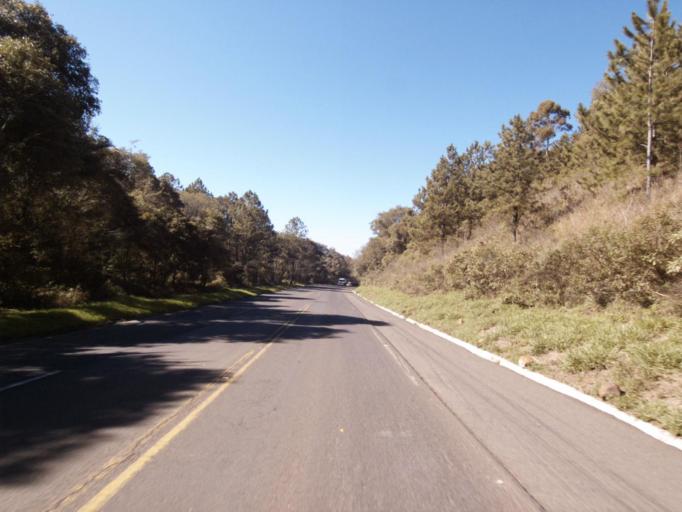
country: BR
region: Santa Catarina
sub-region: Sao Lourenco Do Oeste
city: Sao Lourenco dOeste
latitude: -26.8198
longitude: -53.1563
